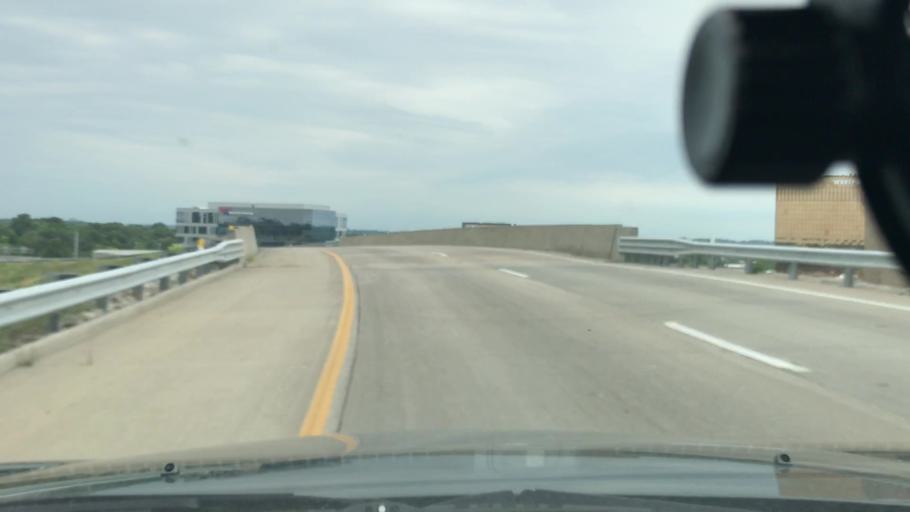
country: US
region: Missouri
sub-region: Saint Louis County
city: Maryland Heights
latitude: 38.6983
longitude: -90.4481
